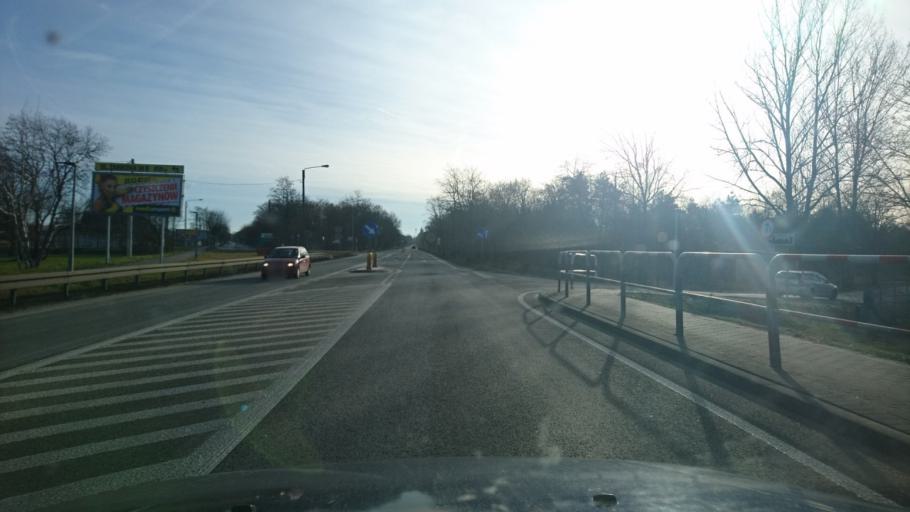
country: PL
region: Greater Poland Voivodeship
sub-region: Powiat ostrzeszowski
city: Ostrzeszow
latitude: 51.4349
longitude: 17.9159
